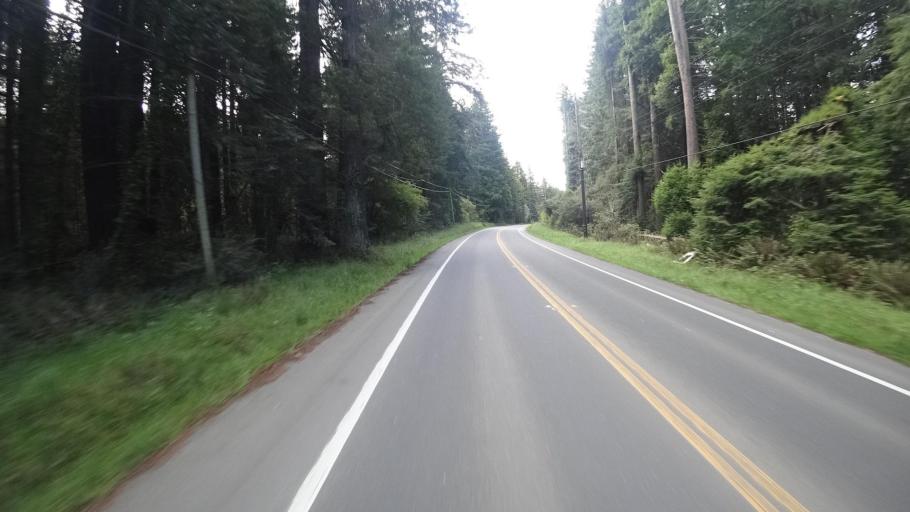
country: US
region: California
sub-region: Humboldt County
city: Myrtletown
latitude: 40.7771
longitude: -124.0738
